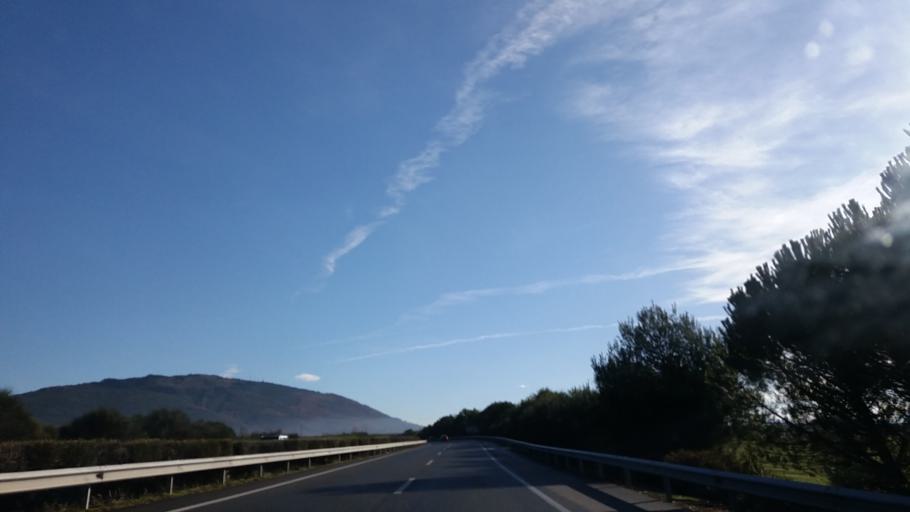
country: ES
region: Navarre
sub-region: Provincia de Navarra
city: Berriobeiti
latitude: 42.8546
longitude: -1.7212
